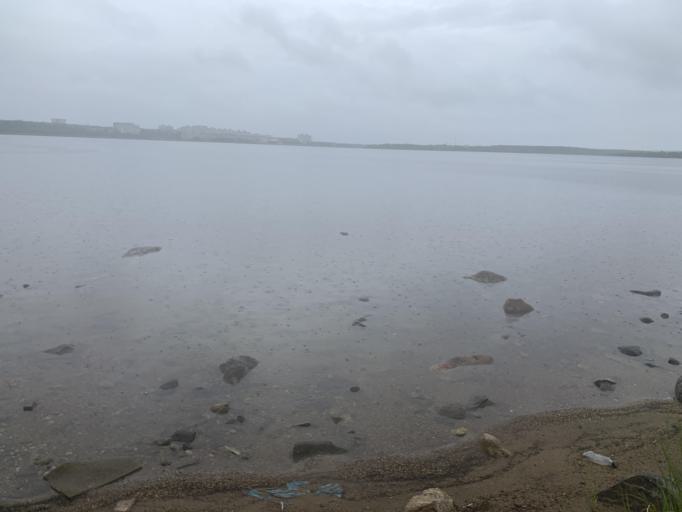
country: RU
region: Murmansk
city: Monchegorsk
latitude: 67.9373
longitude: 32.9896
